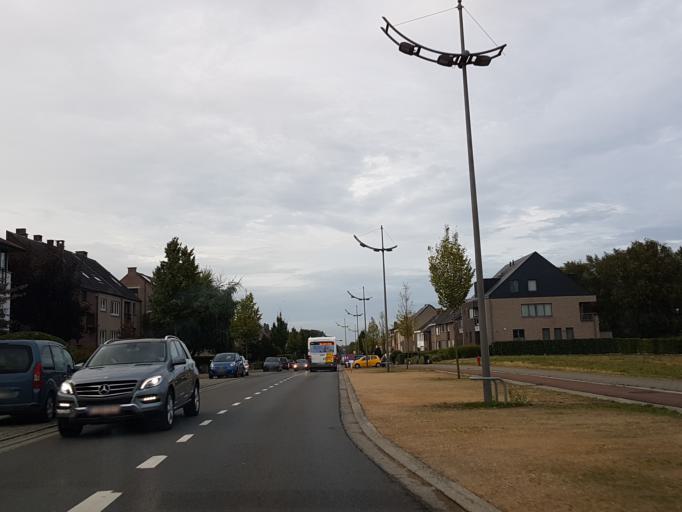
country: BE
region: Flanders
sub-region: Provincie Vlaams-Brabant
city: Kraainem
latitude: 50.8528
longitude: 4.4645
